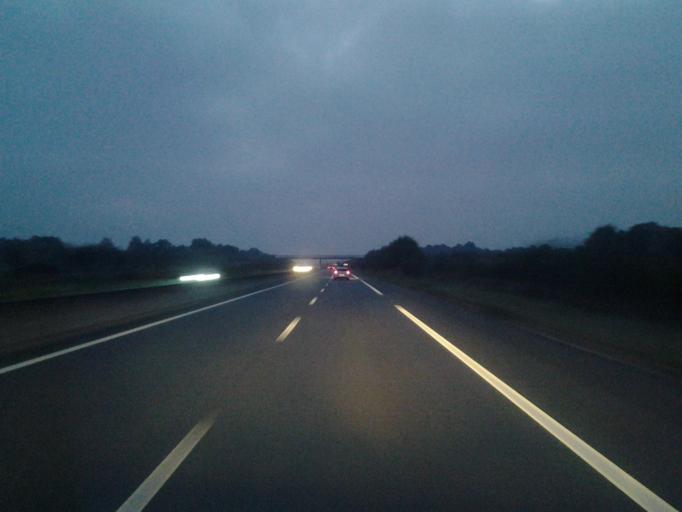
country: FR
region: Pays de la Loire
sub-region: Departement de la Vendee
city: Les Clouzeaux
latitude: 46.6337
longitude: -1.4829
